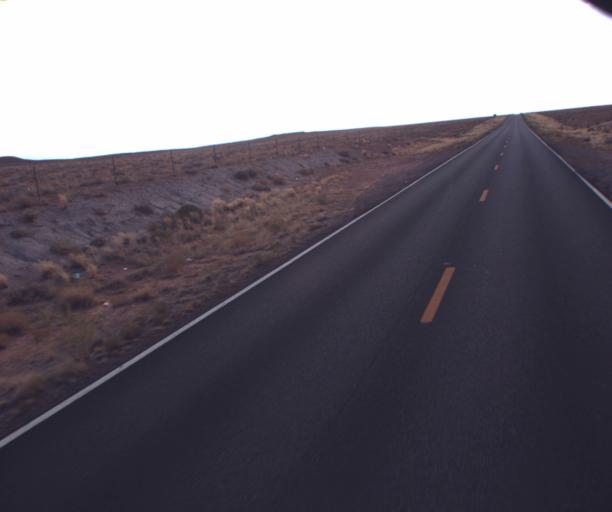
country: US
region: Arizona
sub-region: Apache County
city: Many Farms
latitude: 36.5795
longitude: -109.5540
